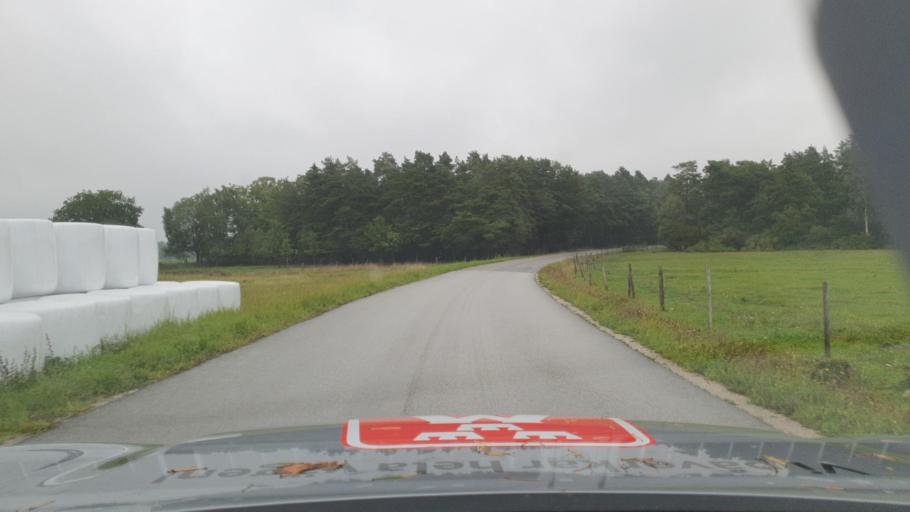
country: SE
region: Gotland
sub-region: Gotland
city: Visby
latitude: 57.7567
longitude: 18.5286
